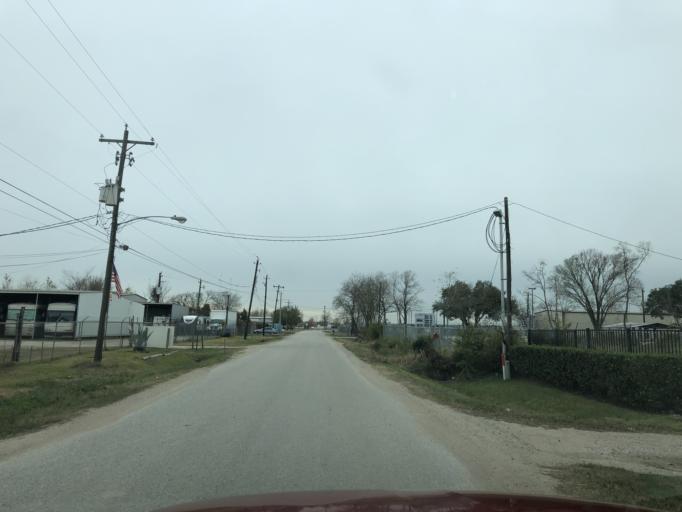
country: US
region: Texas
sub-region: Fort Bend County
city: Missouri City
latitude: 29.6341
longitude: -95.5224
